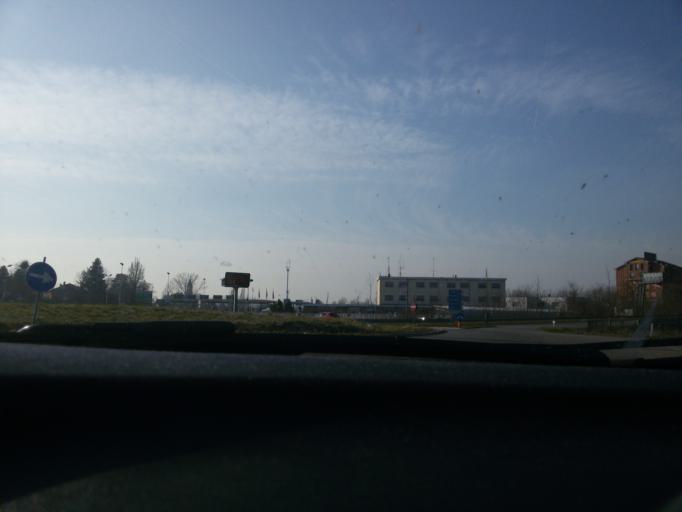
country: IT
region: Piedmont
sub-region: Provincia di Alessandria
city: Alessandria
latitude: 44.9360
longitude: 8.5861
